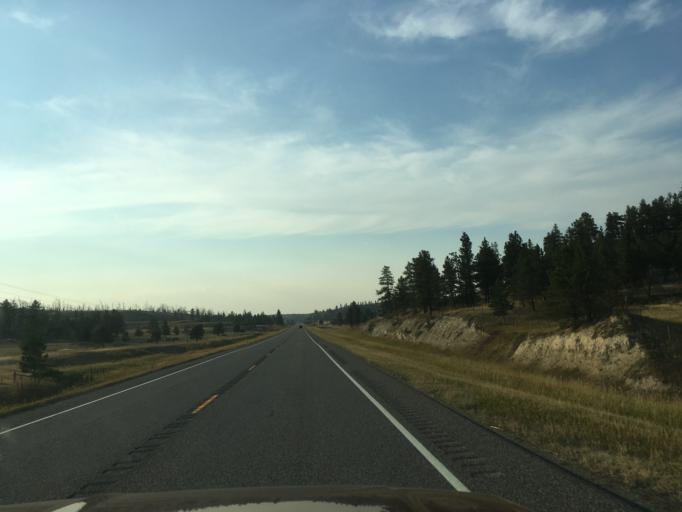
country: US
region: Montana
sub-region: Musselshell County
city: Roundup
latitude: 46.2834
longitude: -108.4782
